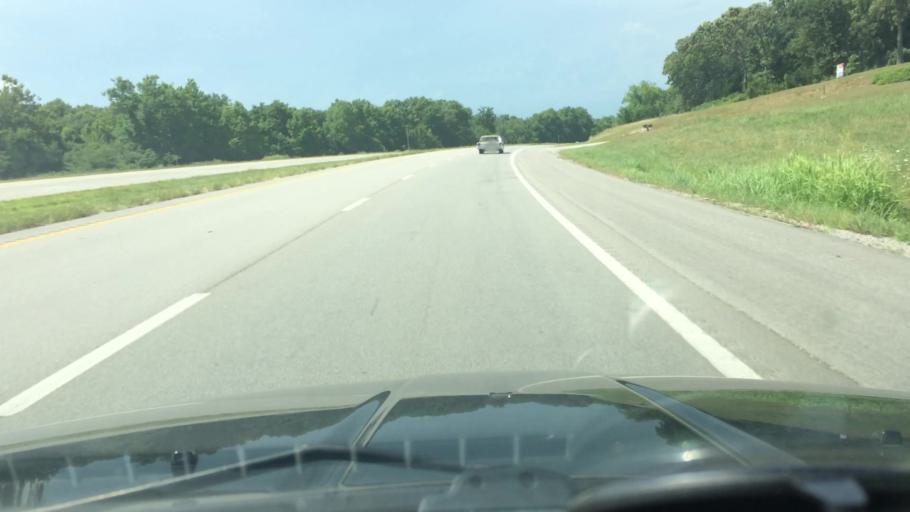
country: US
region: Missouri
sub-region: Henry County
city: Clinton
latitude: 38.2147
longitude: -93.7598
